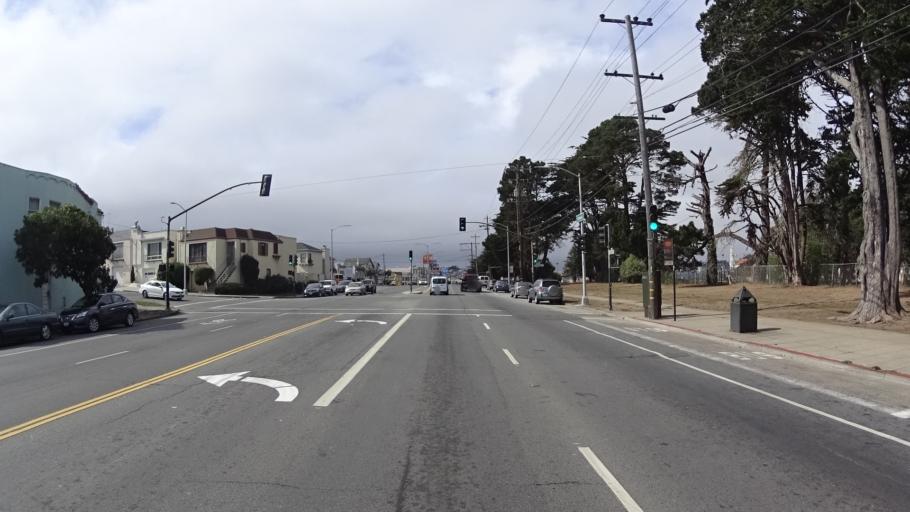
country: US
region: California
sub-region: San Mateo County
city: Daly City
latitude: 37.7127
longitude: -122.4314
